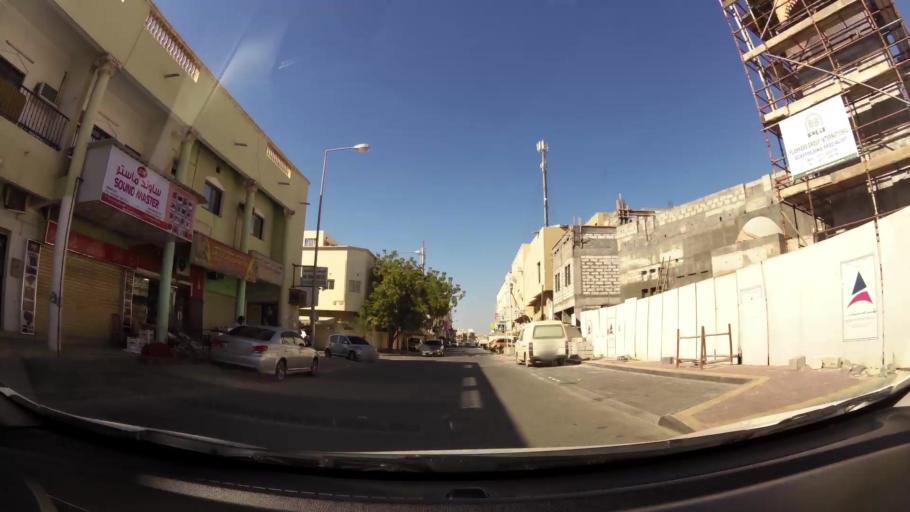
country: BH
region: Muharraq
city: Al Hadd
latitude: 26.2384
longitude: 50.6554
